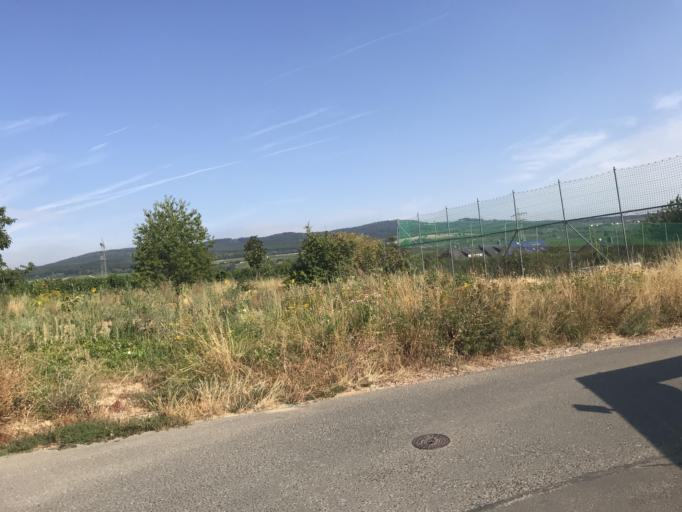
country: DE
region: Rheinland-Pfalz
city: Oestrich-Winkel
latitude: 50.0089
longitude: 8.0194
